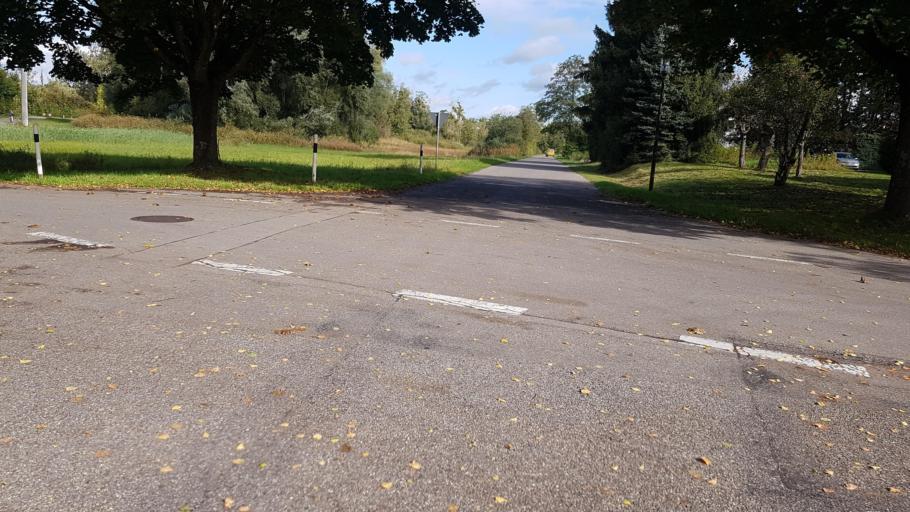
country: DE
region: Baden-Wuerttemberg
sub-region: Tuebingen Region
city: Eriskirch
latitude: 47.6208
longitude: 9.5331
